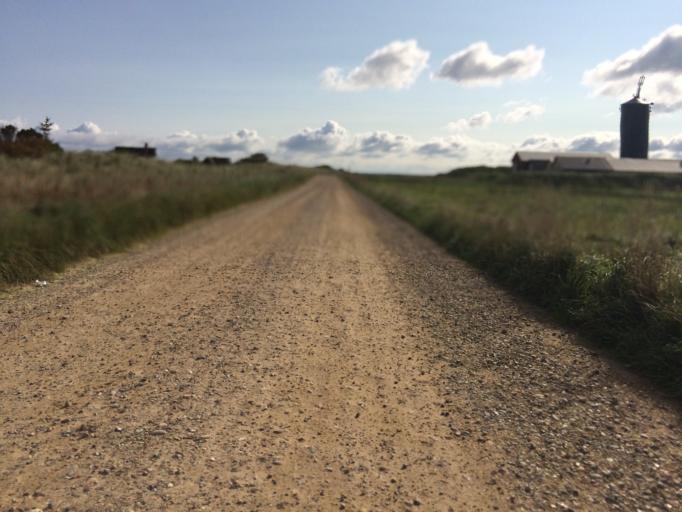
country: DK
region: Central Jutland
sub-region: Ringkobing-Skjern Kommune
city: Hvide Sande
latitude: 55.8867
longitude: 8.1699
